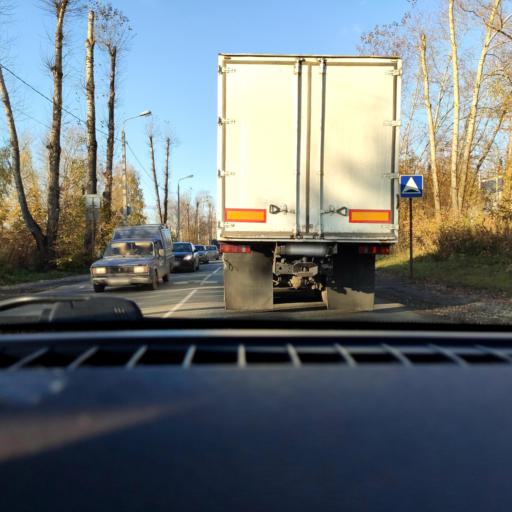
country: RU
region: Perm
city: Kondratovo
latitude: 57.9676
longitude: 56.1278
